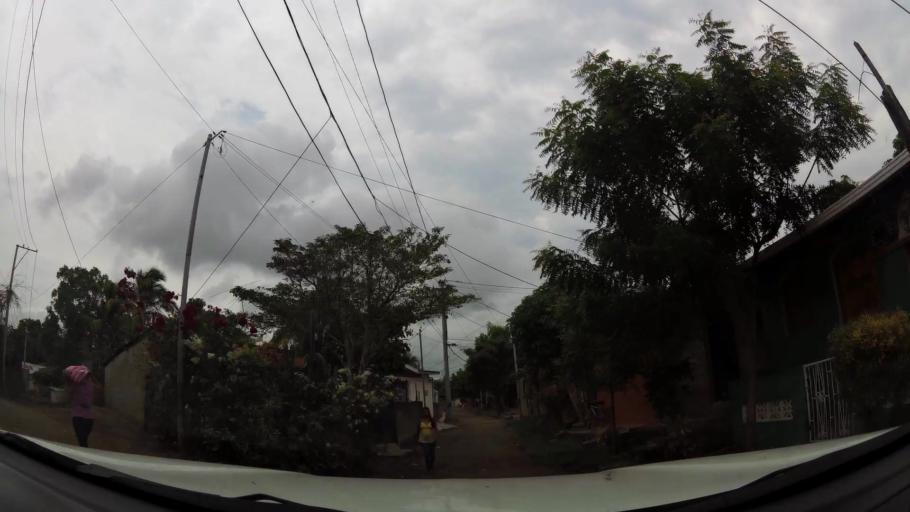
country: NI
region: Granada
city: Granada
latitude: 11.9349
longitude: -85.9472
